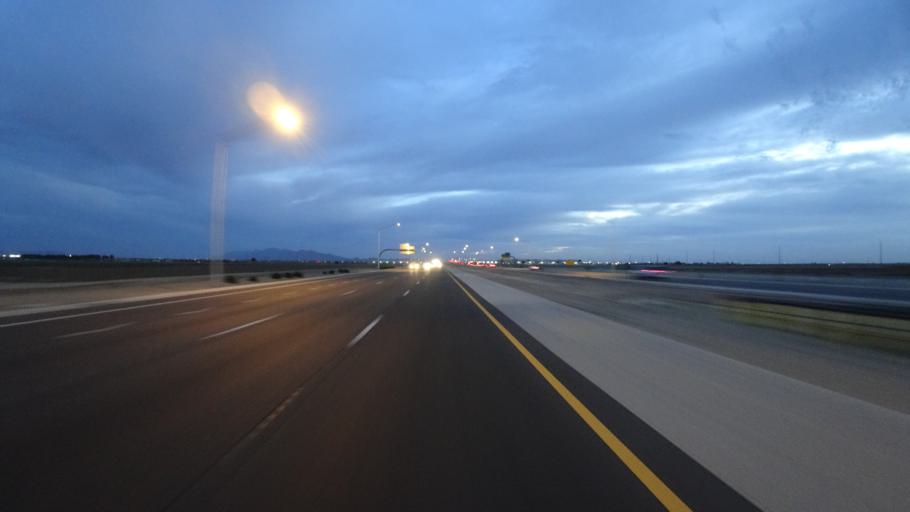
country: US
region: Arizona
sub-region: Maricopa County
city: Citrus Park
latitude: 33.5156
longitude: -112.4185
